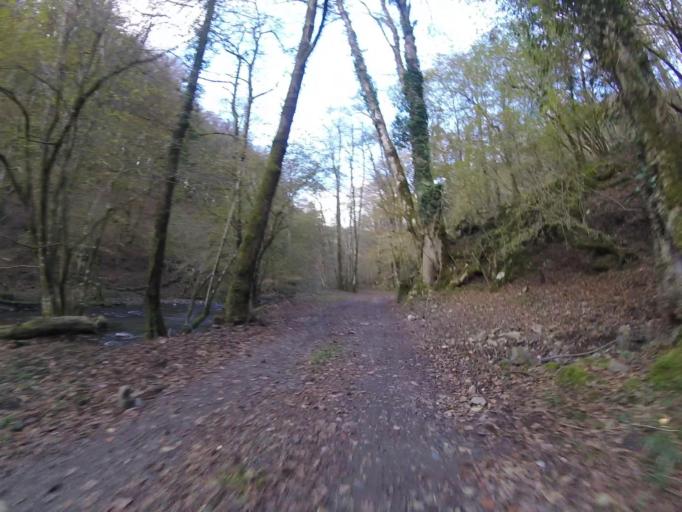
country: ES
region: Navarre
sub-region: Provincia de Navarra
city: Goizueta
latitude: 43.2034
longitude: -1.8071
